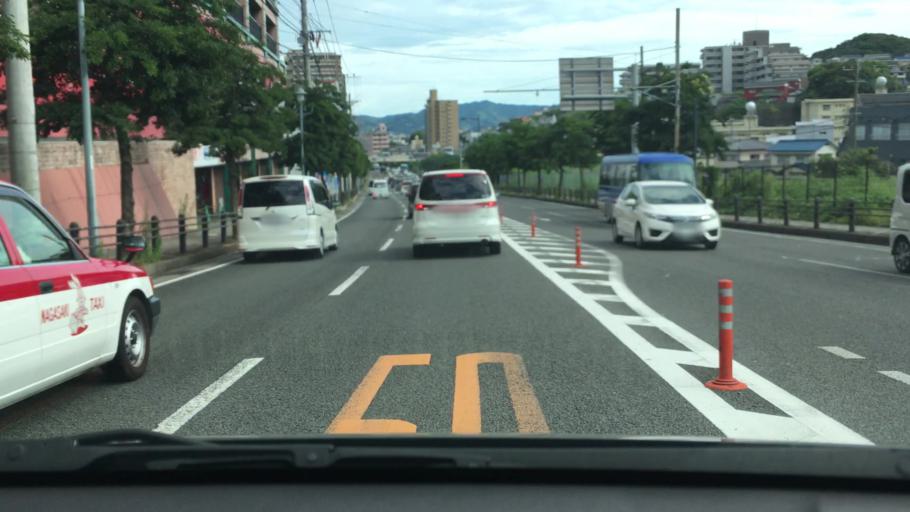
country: JP
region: Nagasaki
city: Togitsu
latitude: 32.8002
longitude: 129.8535
